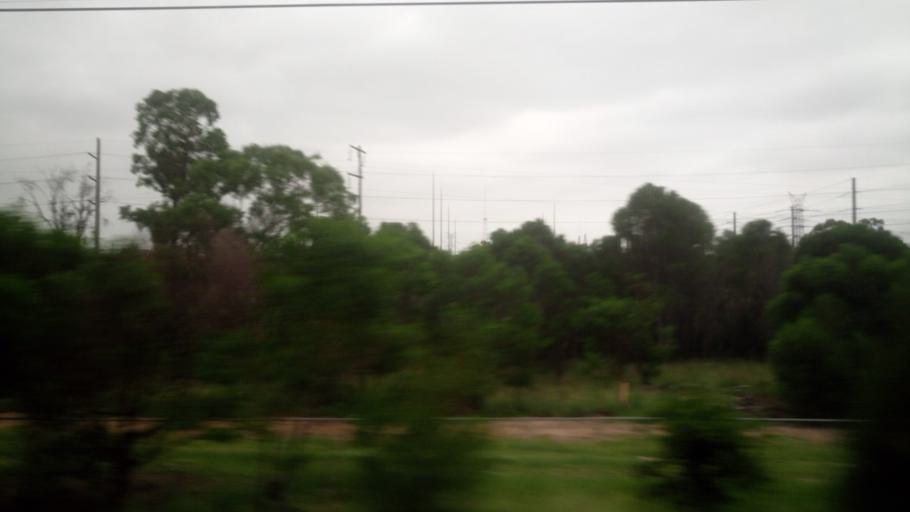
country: AU
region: New South Wales
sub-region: Blacktown
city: Mount Druitt
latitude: -33.7648
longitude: 150.7920
